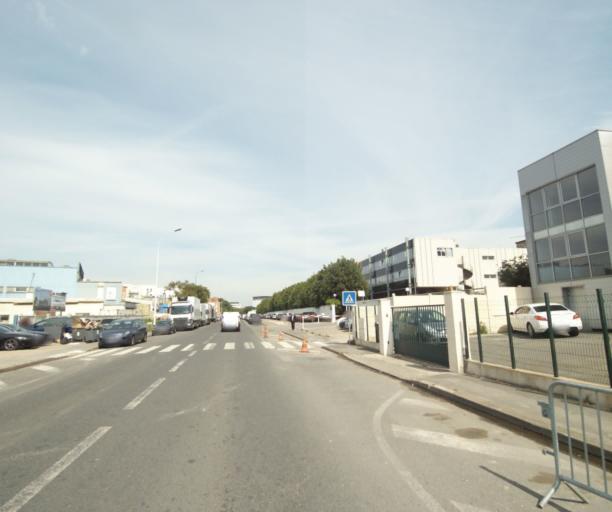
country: FR
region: Ile-de-France
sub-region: Departement des Hauts-de-Seine
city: Gennevilliers
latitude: 48.9302
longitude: 2.3083
